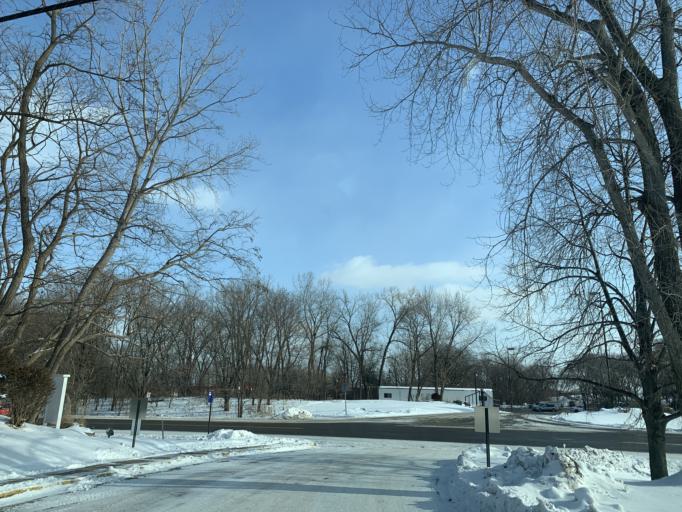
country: US
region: Minnesota
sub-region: Dakota County
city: Inver Grove Heights
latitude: 44.8715
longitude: -93.0651
